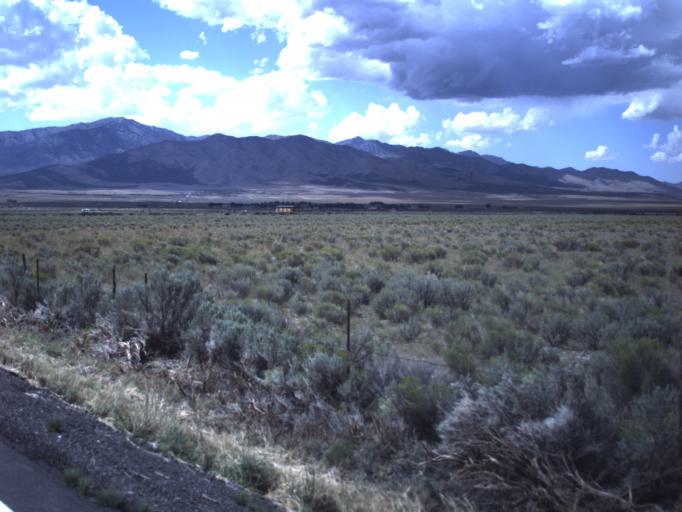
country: US
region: Utah
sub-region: Tooele County
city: Tooele
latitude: 40.3369
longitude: -112.4188
